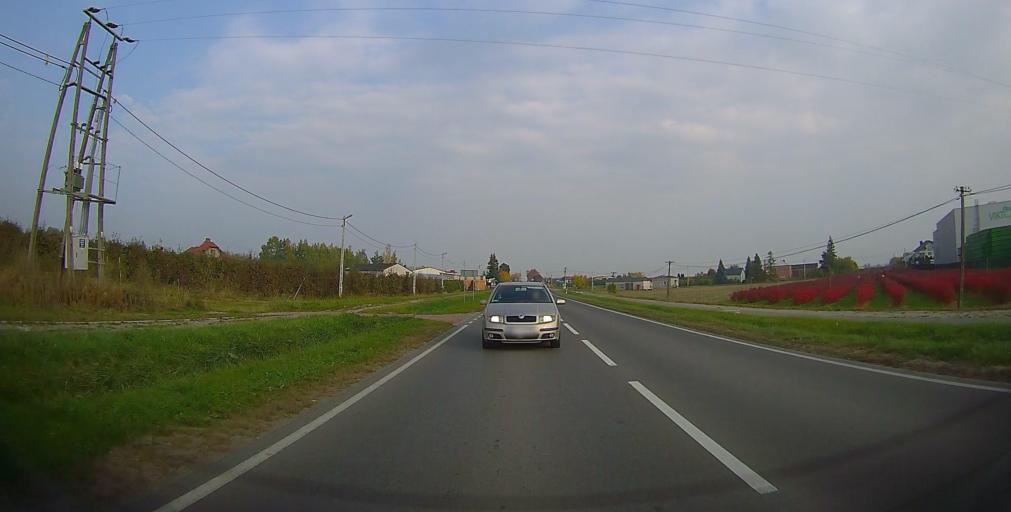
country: PL
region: Masovian Voivodeship
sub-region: Powiat grojecki
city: Mogielnica
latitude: 51.7483
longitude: 20.7636
